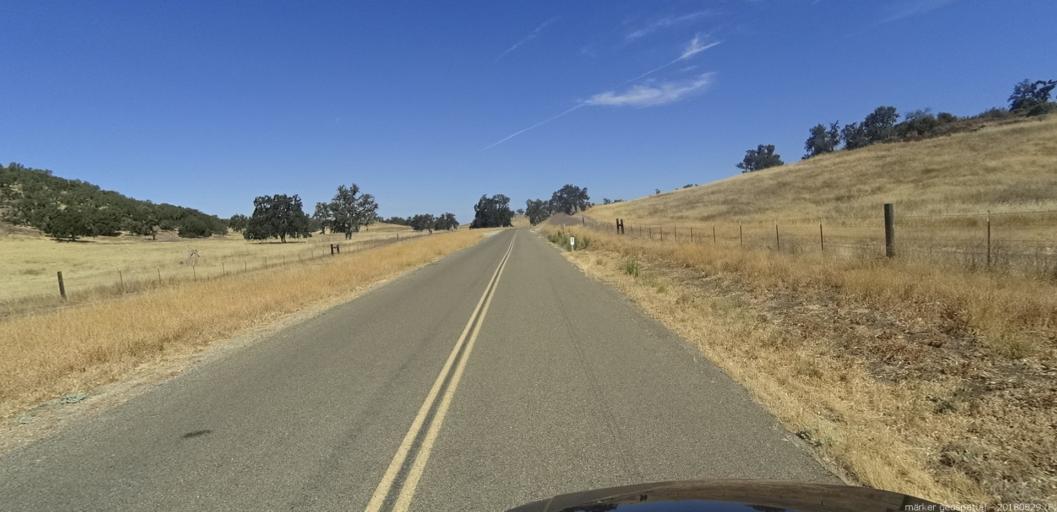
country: US
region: California
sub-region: San Luis Obispo County
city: Lake Nacimiento
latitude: 35.8310
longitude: -120.9764
